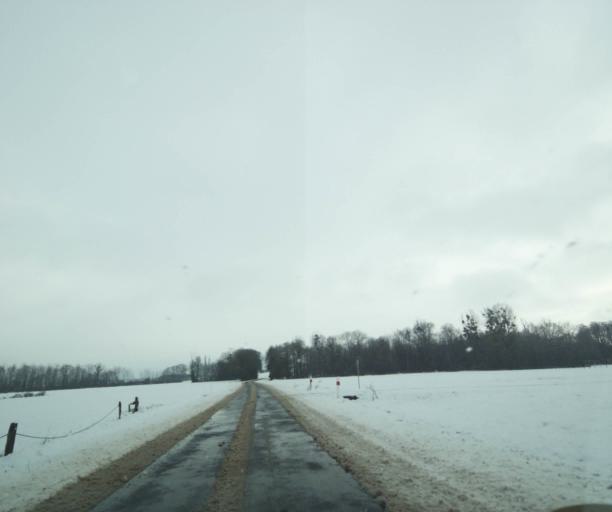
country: FR
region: Champagne-Ardenne
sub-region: Departement de la Haute-Marne
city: Montier-en-Der
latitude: 48.4948
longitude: 4.7065
